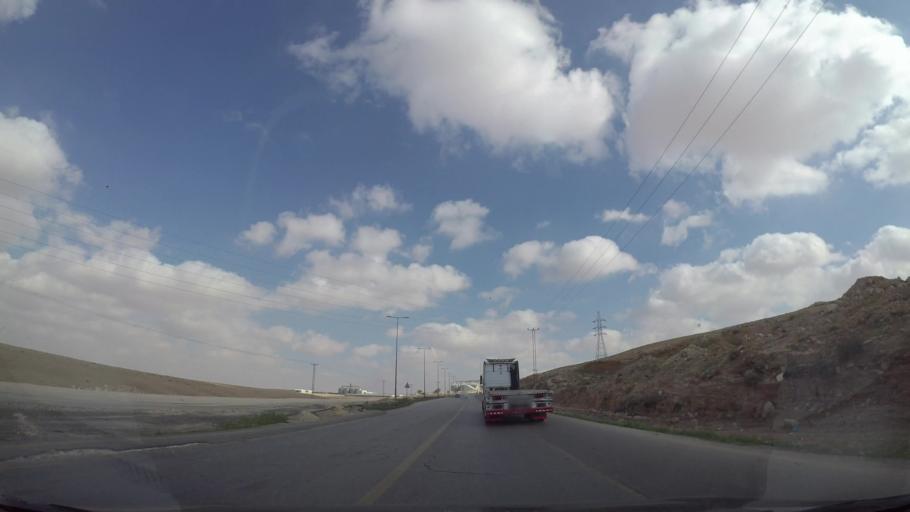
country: JO
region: Amman
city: Al Jizah
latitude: 31.6278
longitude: 35.9889
